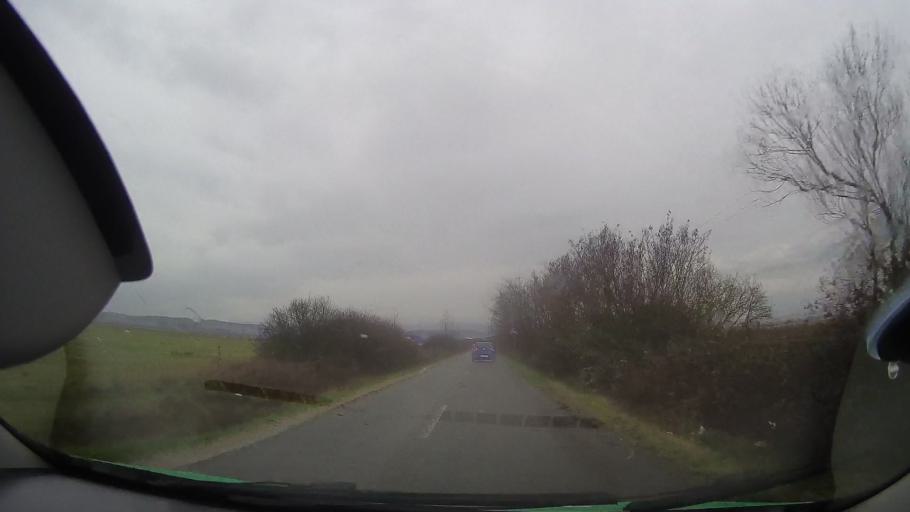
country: RO
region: Bihor
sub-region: Comuna Holod
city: Vintere
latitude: 46.7572
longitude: 22.1479
